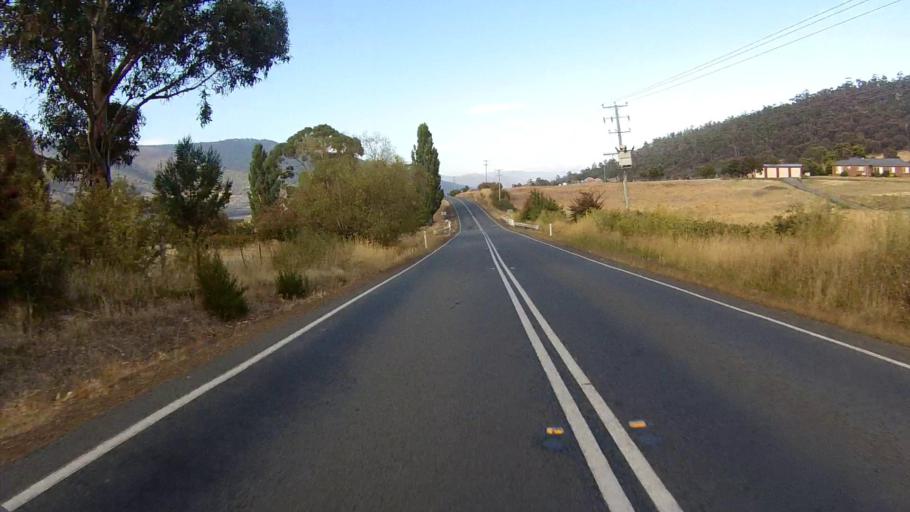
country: AU
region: Tasmania
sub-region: Brighton
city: Bridgewater
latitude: -42.7347
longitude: 147.1752
